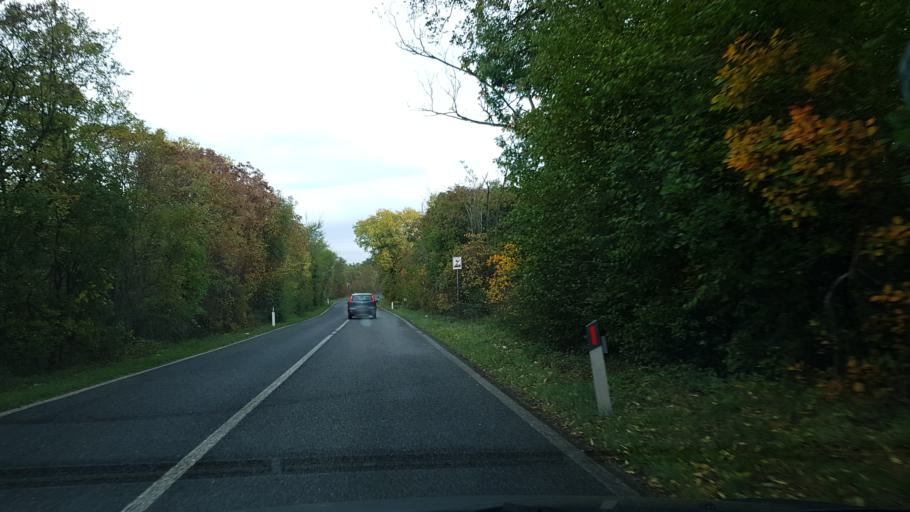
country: IT
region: Friuli Venezia Giulia
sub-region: Provincia di Gorizia
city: Doberdo del Lago
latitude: 45.8506
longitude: 13.5399
